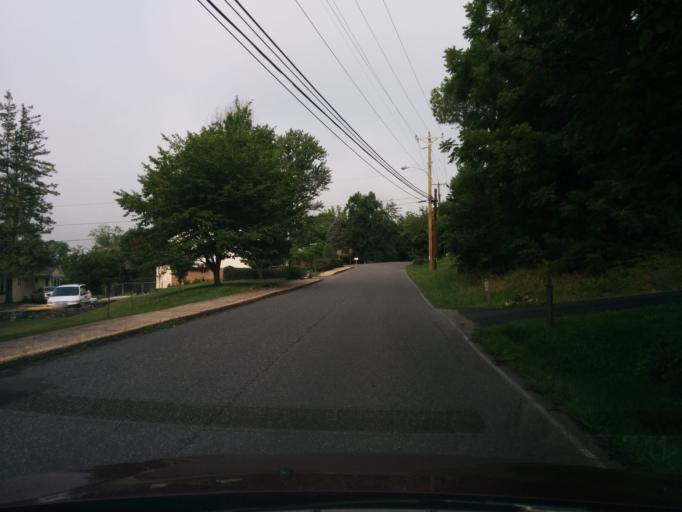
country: US
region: Virginia
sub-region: City of Lexington
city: Lexington
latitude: 37.7858
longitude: -79.4572
